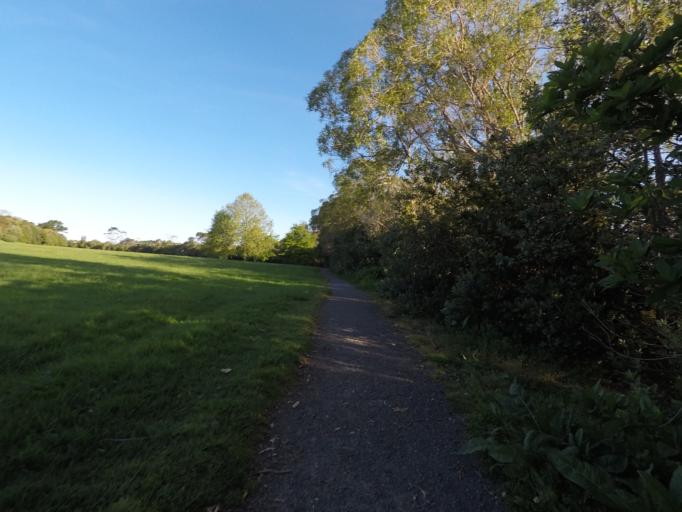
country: NZ
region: Auckland
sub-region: Auckland
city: Rosebank
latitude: -36.8419
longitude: 174.6332
